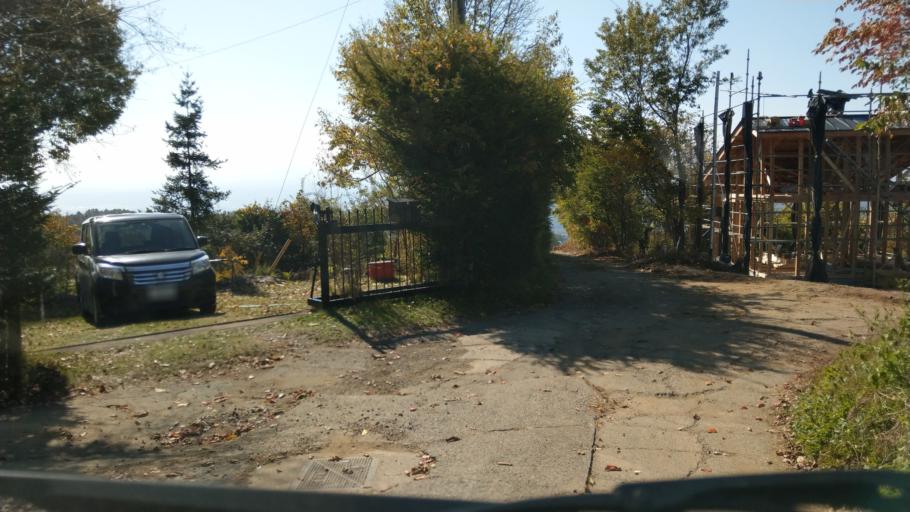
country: JP
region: Nagano
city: Komoro
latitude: 36.3588
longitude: 138.4453
